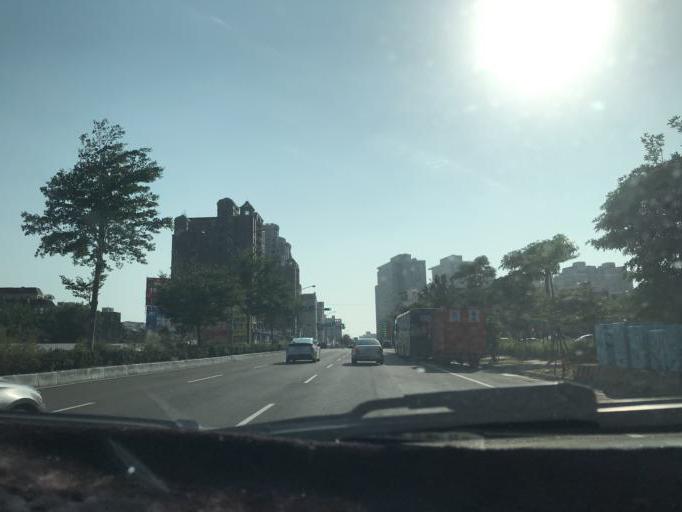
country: TW
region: Taiwan
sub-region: Hsinchu
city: Zhubei
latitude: 24.8247
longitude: 121.0322
